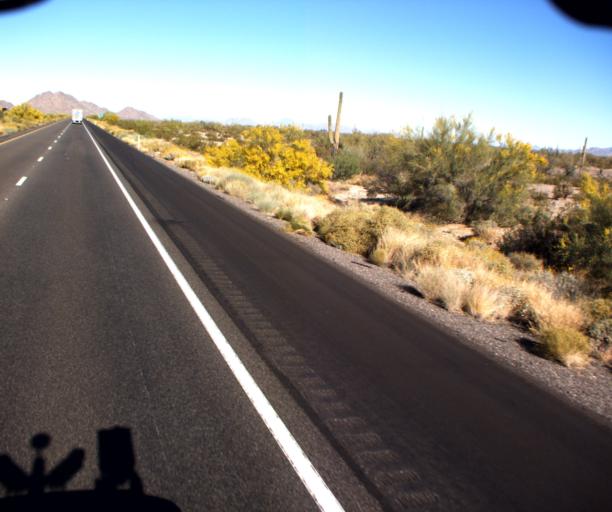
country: US
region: Arizona
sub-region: Maricopa County
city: Gila Bend
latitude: 32.8946
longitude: -112.4960
